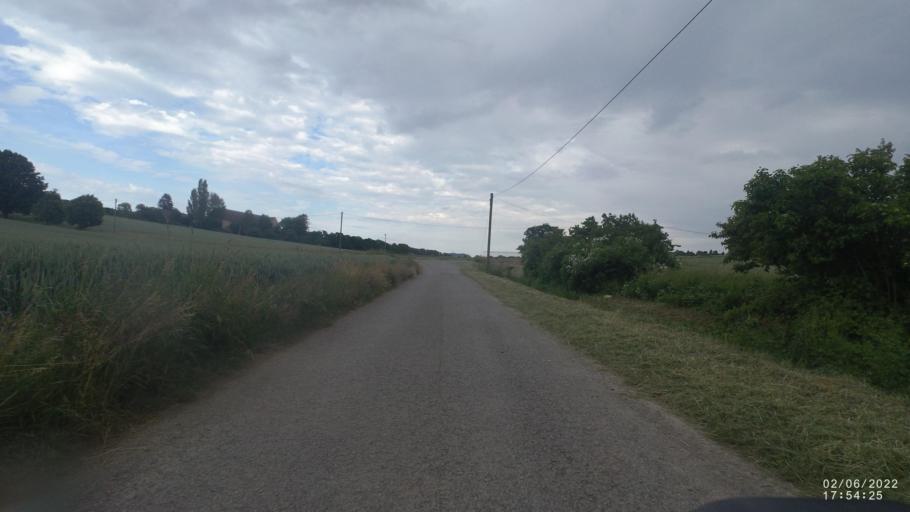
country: DE
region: Baden-Wuerttemberg
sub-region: Regierungsbezirk Stuttgart
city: Stuttgart Muehlhausen
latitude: 48.8487
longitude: 9.2646
